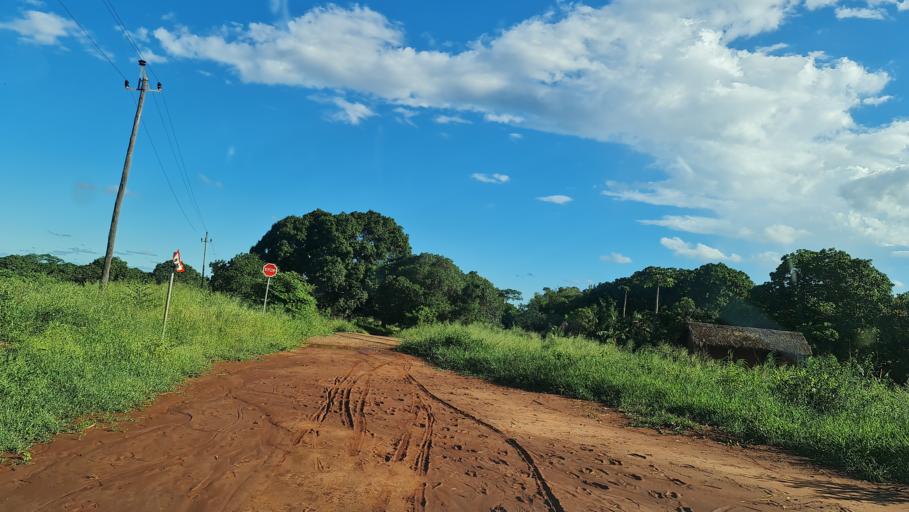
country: MZ
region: Nampula
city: Ilha de Mocambique
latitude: -14.9229
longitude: 40.2186
